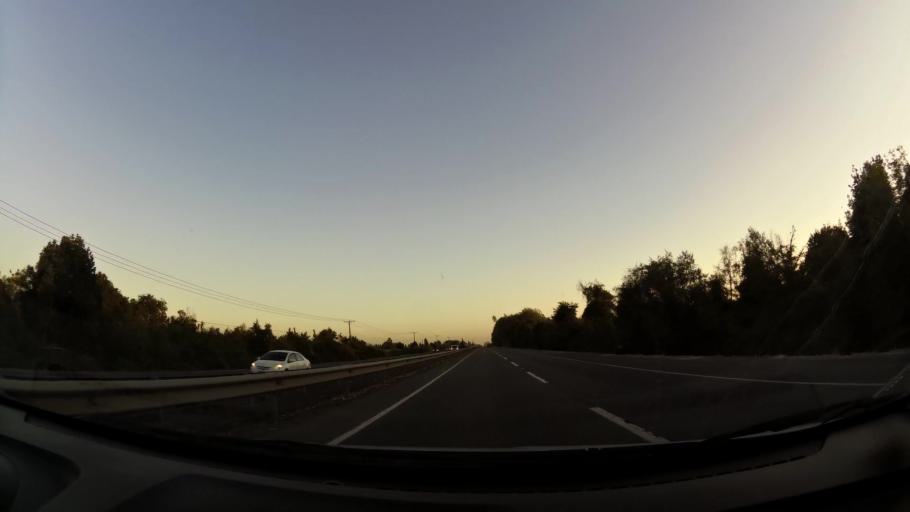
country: CL
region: Maule
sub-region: Provincia de Linares
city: San Javier
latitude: -35.6472
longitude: -71.6962
